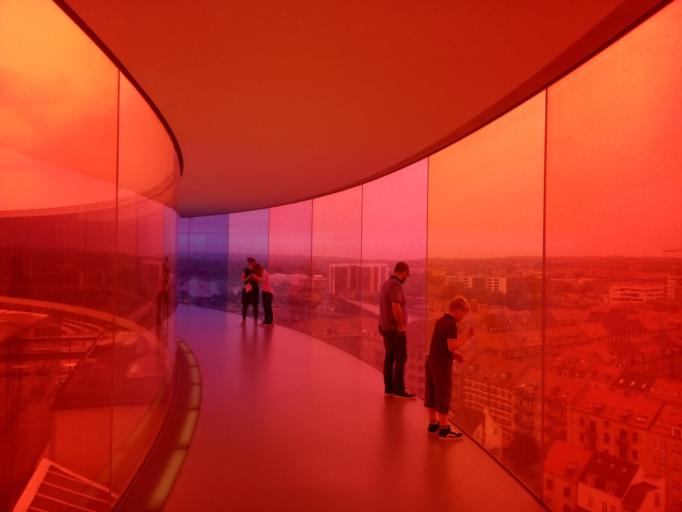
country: DK
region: Central Jutland
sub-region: Arhus Kommune
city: Arhus
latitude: 56.1541
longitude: 10.1996
